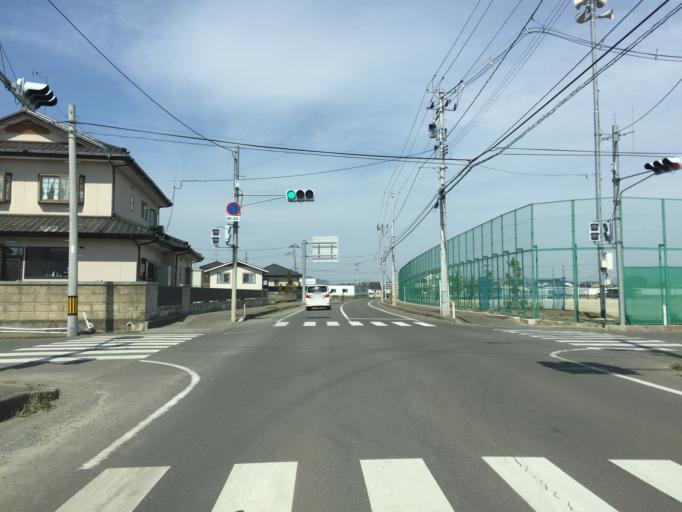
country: JP
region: Miyagi
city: Watari
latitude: 38.0417
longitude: 140.9096
